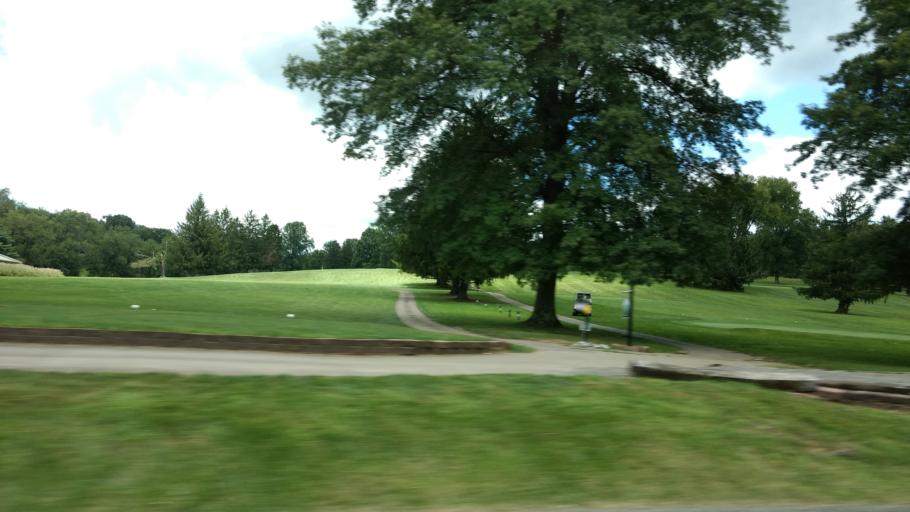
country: US
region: Pennsylvania
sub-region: Westmoreland County
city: Murrysville
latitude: 40.4455
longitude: -79.6804
